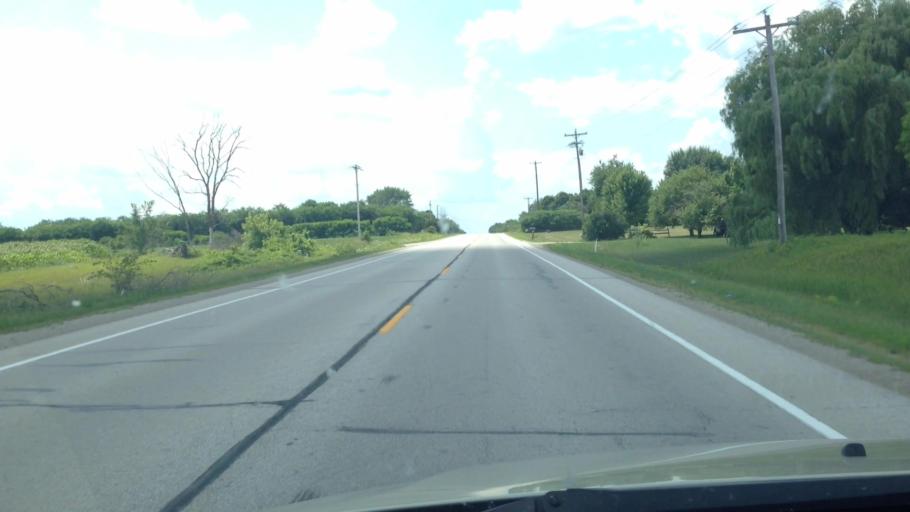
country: US
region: Wisconsin
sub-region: Brown County
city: Suamico
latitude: 44.6479
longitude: -88.1344
